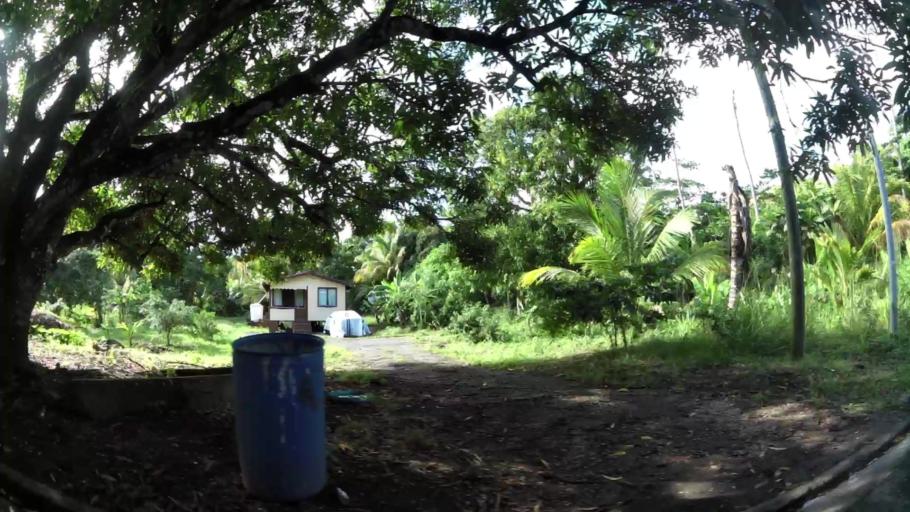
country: AG
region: Saint Peter
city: All Saints
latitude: 17.0473
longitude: -61.8126
